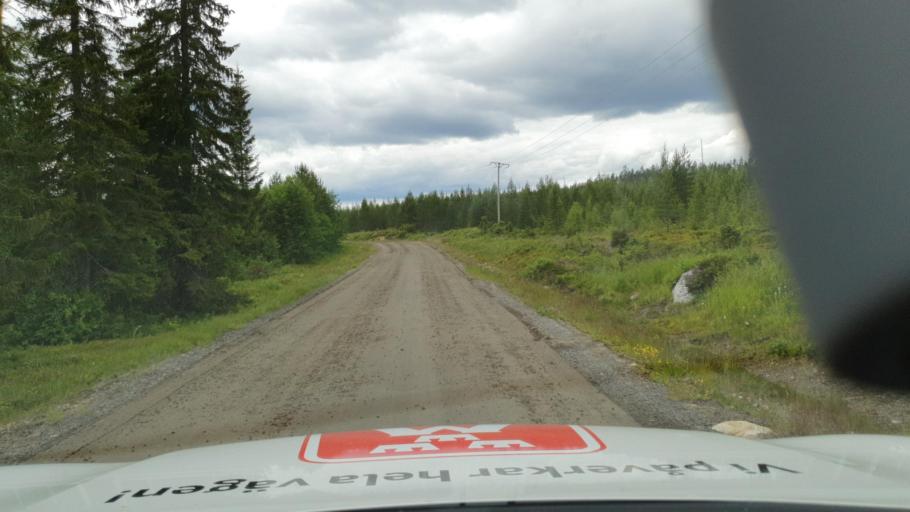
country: SE
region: Vaesterbotten
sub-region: Bjurholms Kommun
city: Bjurholm
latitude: 63.8093
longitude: 19.0679
